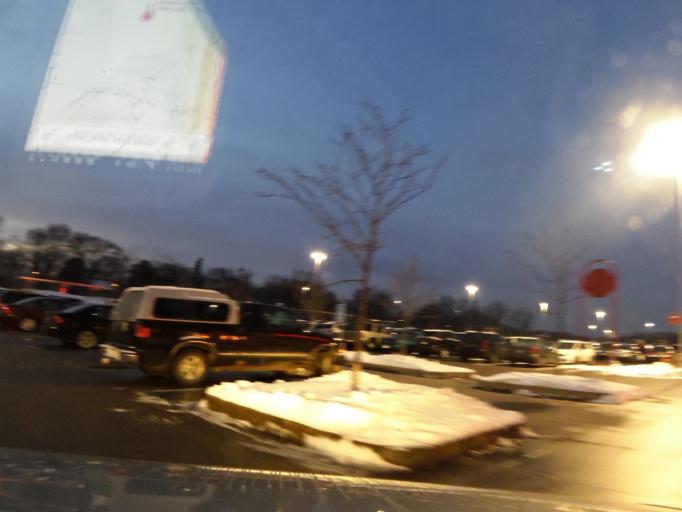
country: US
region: Minnesota
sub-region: Hennepin County
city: Richfield
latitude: 44.8853
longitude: -93.2491
